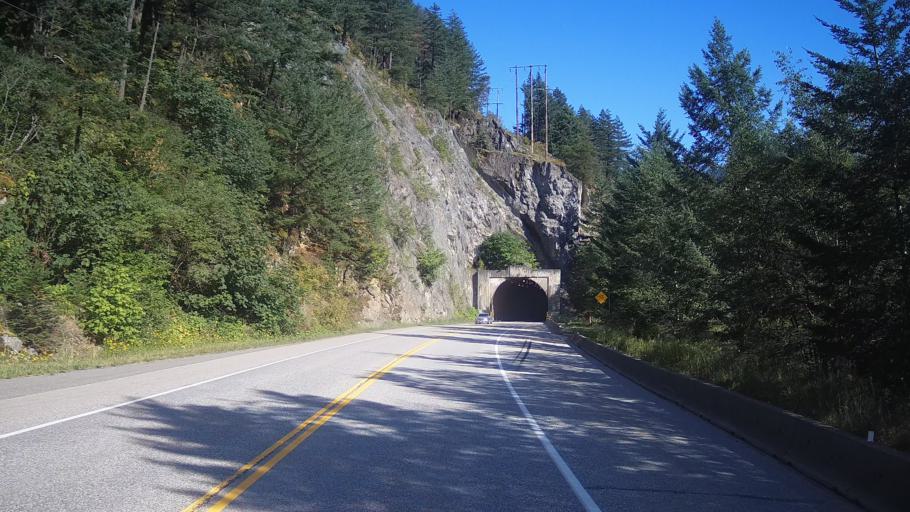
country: CA
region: British Columbia
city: Hope
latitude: 49.5894
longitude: -121.4077
